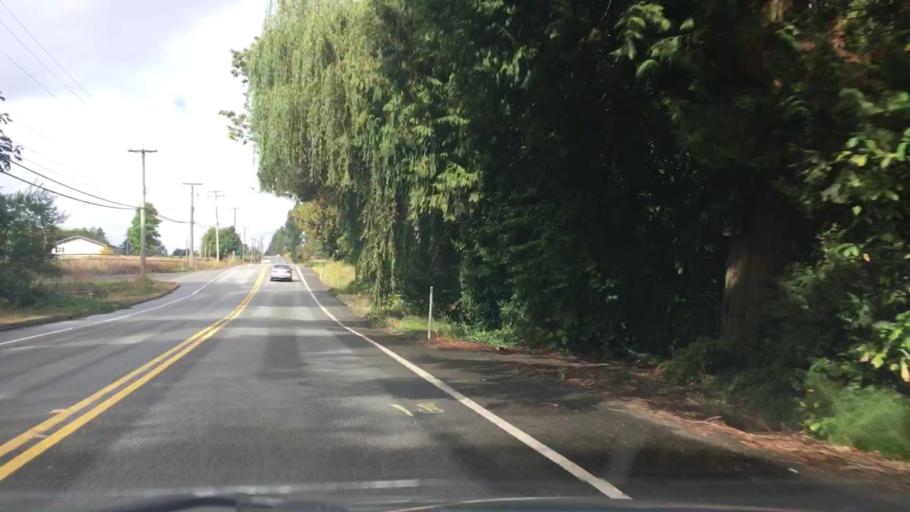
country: CA
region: British Columbia
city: Langley
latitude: 49.1042
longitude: -122.5862
